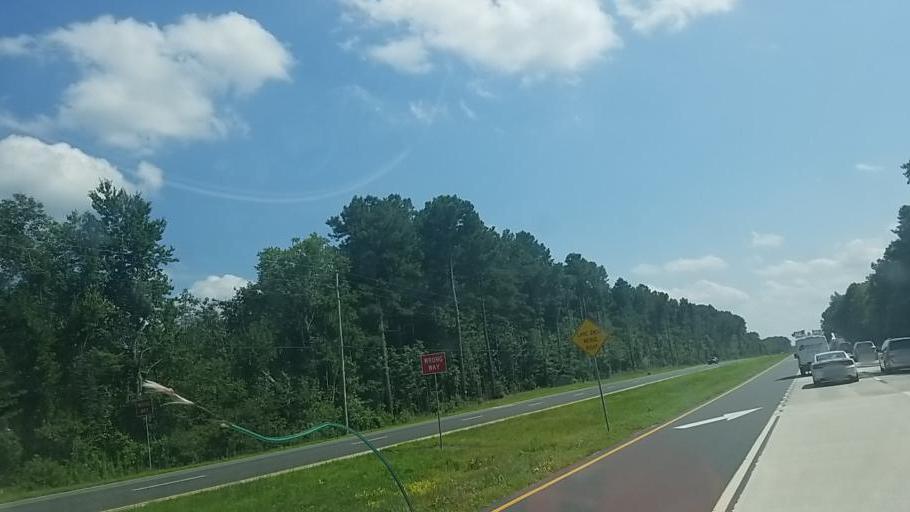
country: US
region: Delaware
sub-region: Sussex County
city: Milford
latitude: 38.8265
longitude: -75.4391
